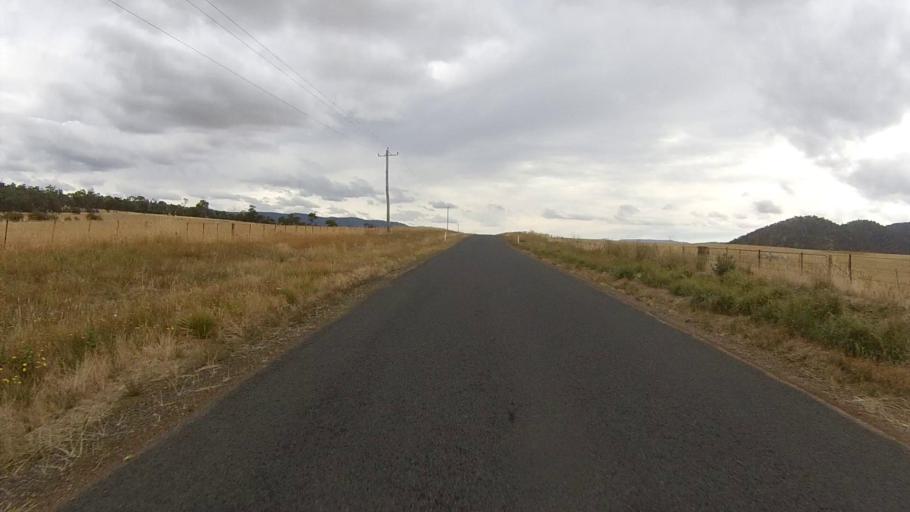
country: AU
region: Tasmania
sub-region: Northern Midlands
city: Evandale
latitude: -41.8252
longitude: 147.8037
